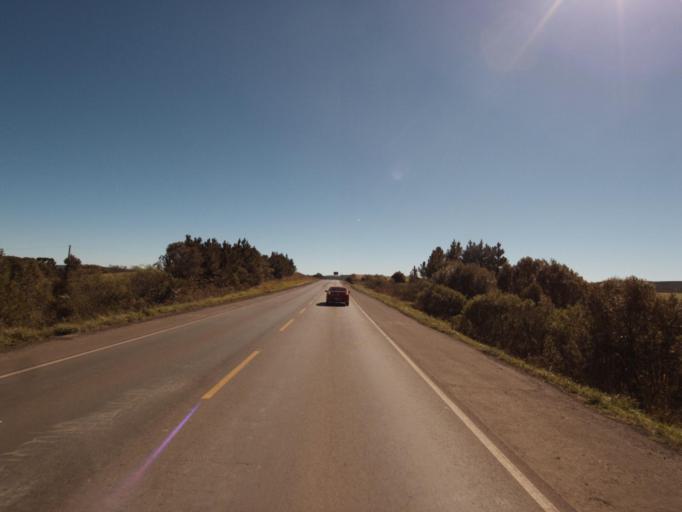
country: BR
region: Santa Catarina
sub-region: Concordia
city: Concordia
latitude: -26.9382
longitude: -51.8679
